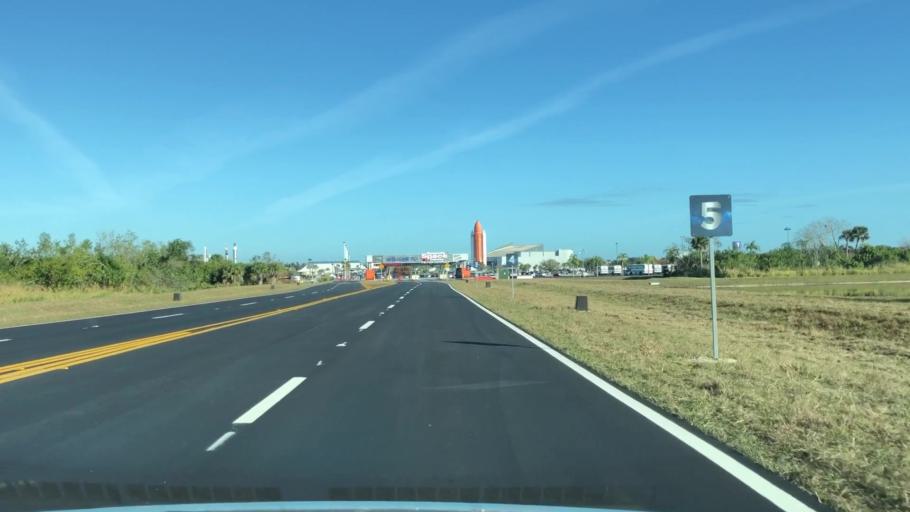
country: US
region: Florida
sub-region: Brevard County
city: Merritt Island
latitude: 28.5168
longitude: -80.6819
